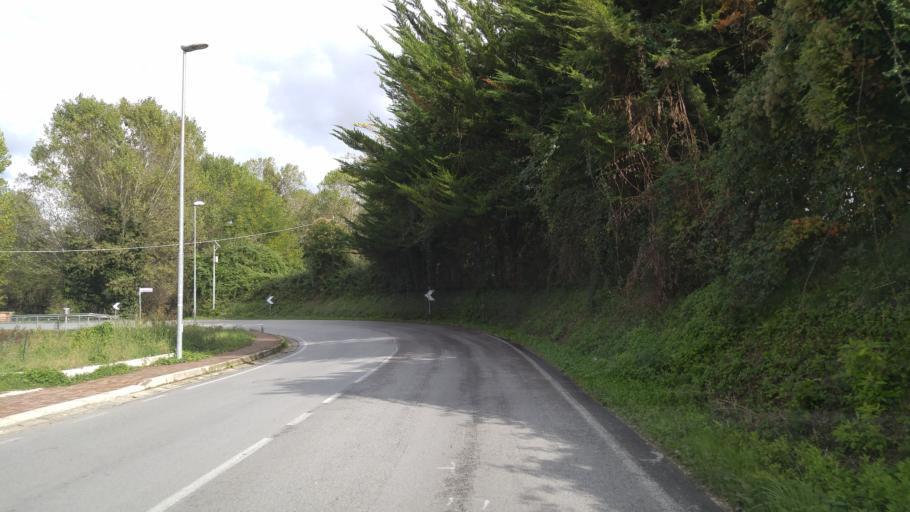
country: IT
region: The Marches
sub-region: Provincia di Pesaro e Urbino
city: Mombaroccio
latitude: 43.8394
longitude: 12.8941
